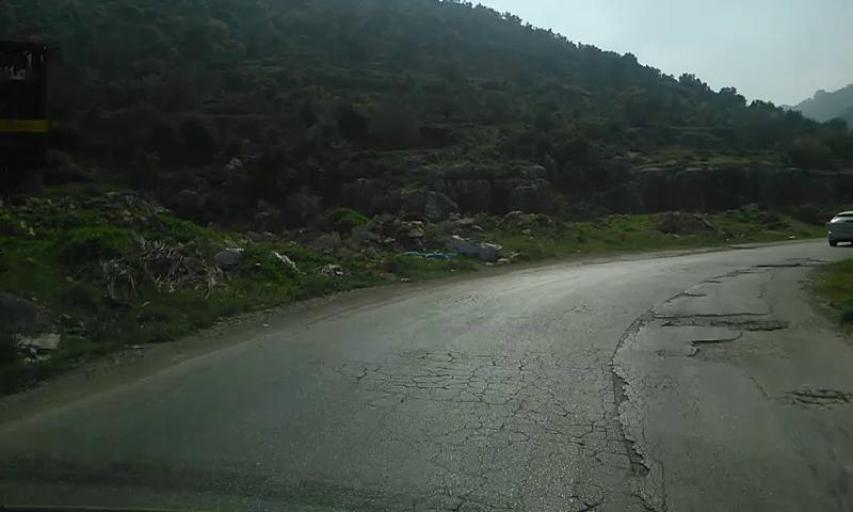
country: PS
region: West Bank
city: Dura al Qar`
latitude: 31.9559
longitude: 35.2373
